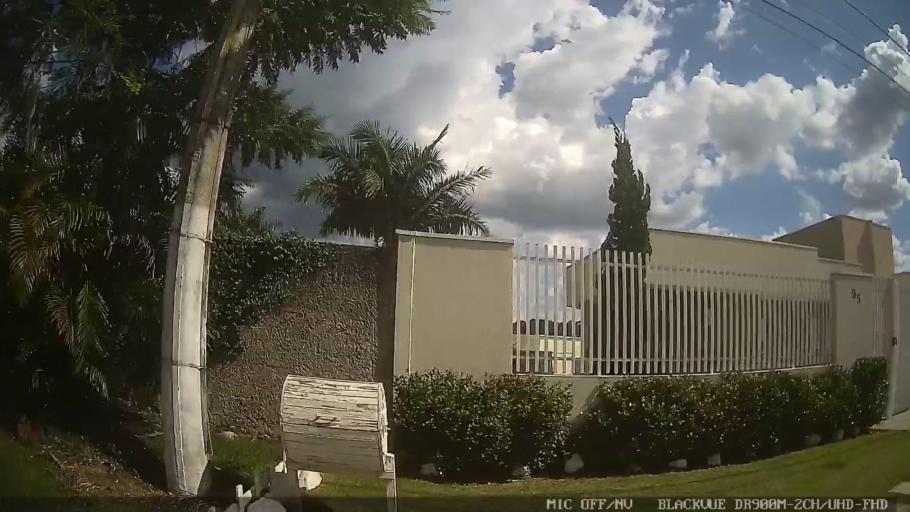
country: BR
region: Sao Paulo
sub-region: Atibaia
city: Atibaia
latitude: -23.1480
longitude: -46.5497
